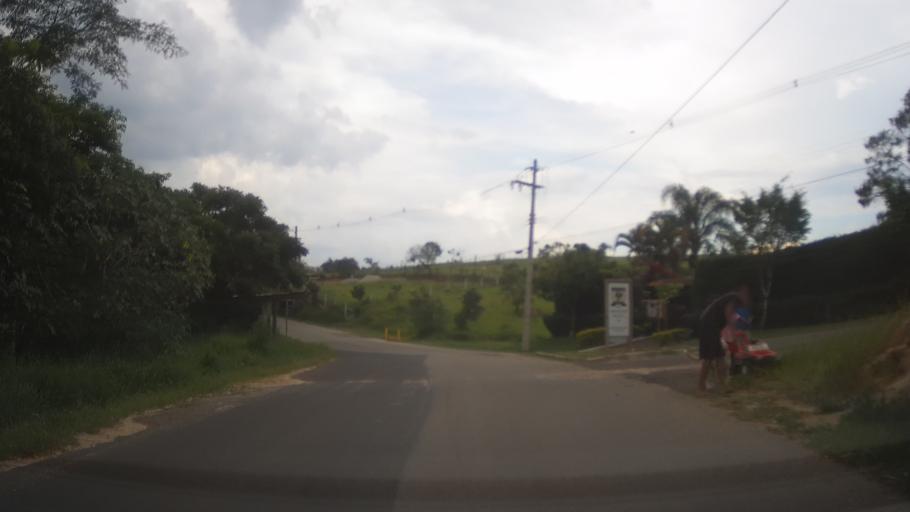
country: BR
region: Sao Paulo
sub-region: Itupeva
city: Itupeva
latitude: -23.1841
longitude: -47.0877
